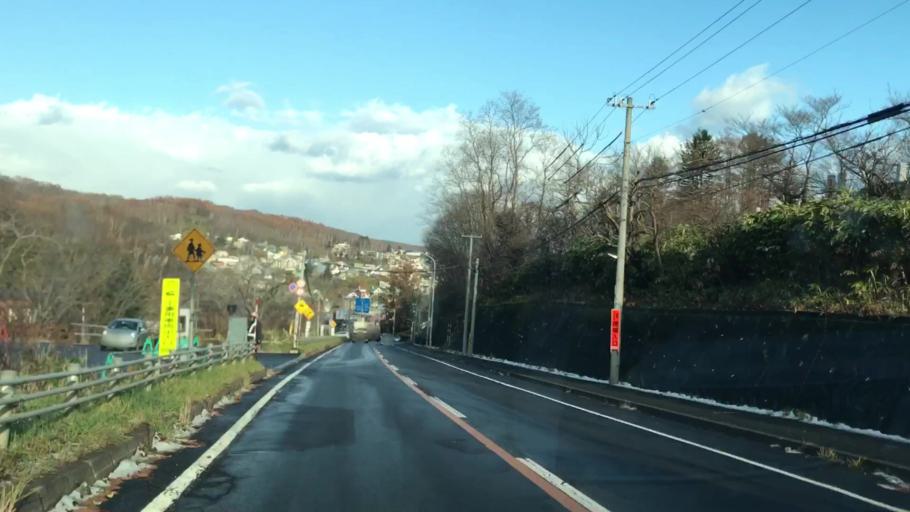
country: JP
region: Hokkaido
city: Otaru
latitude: 43.1653
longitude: 140.9962
